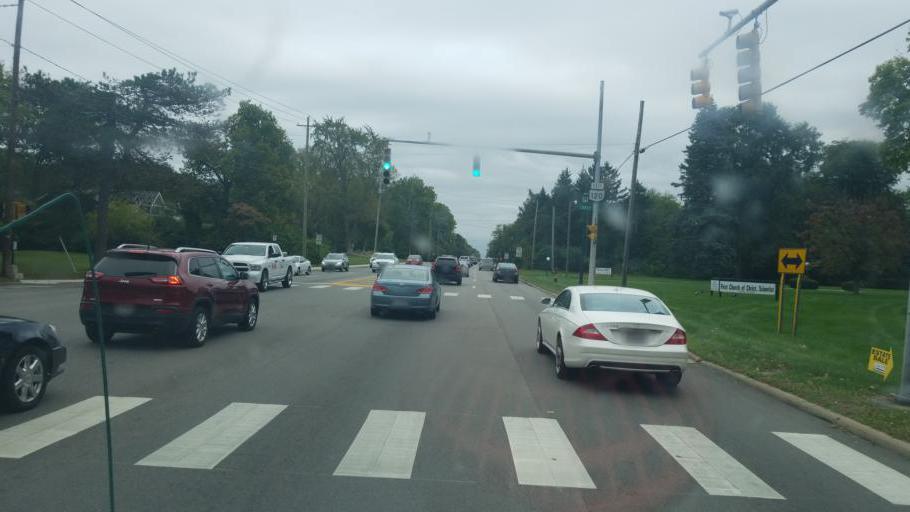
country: US
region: Ohio
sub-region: Lucas County
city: Ottawa Hills
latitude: 41.6770
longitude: -83.6540
